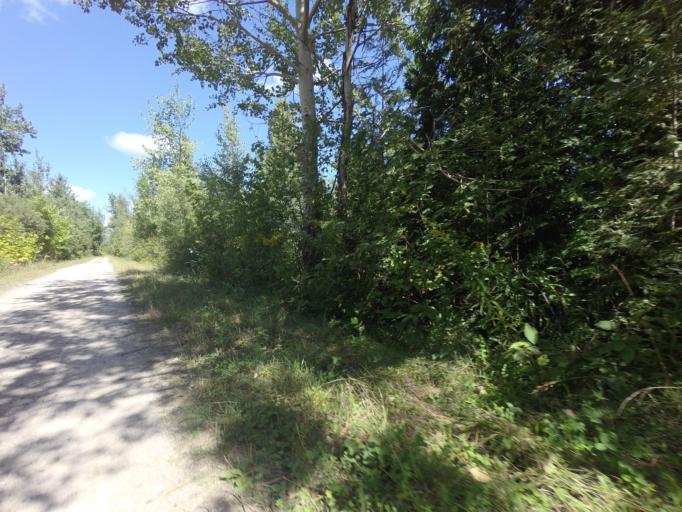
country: CA
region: Ontario
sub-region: Wellington County
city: Guelph
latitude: 43.7615
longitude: -80.3247
